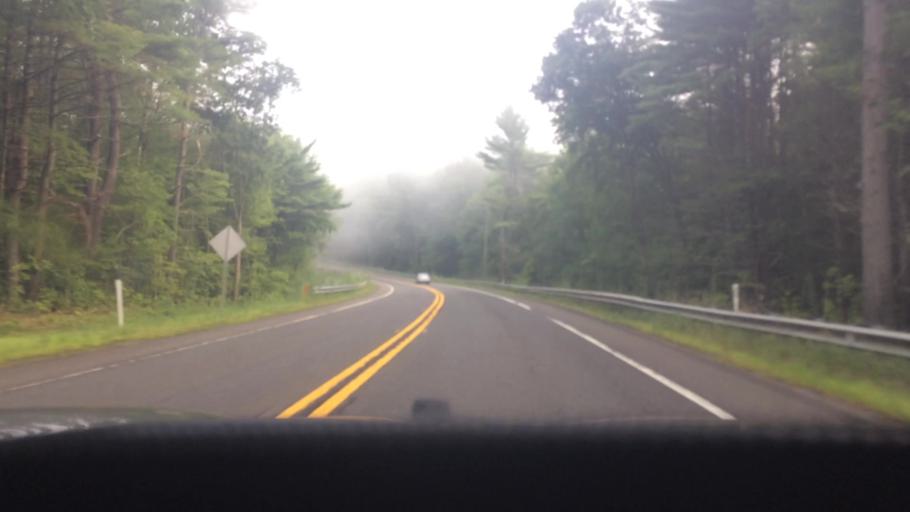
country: US
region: Massachusetts
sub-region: Franklin County
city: Millers Falls
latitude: 42.5932
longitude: -72.4908
